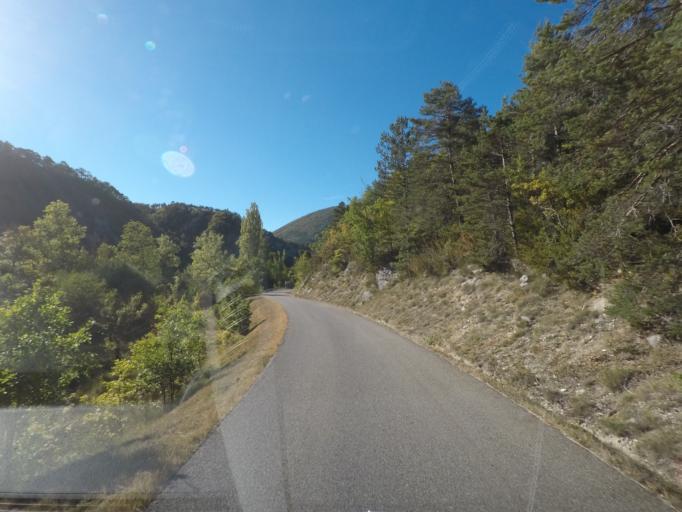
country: FR
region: Provence-Alpes-Cote d'Azur
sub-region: Departement des Hautes-Alpes
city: Serres
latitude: 44.4704
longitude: 5.4636
